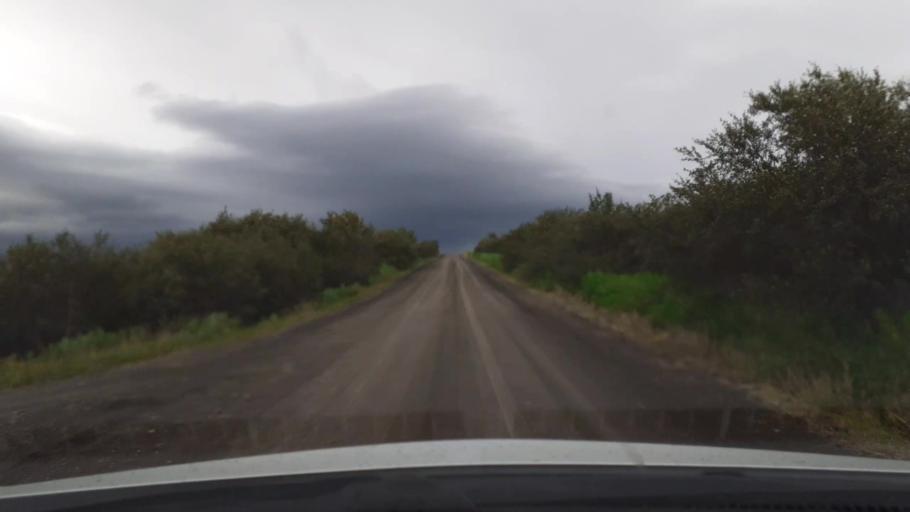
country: IS
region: Capital Region
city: Mosfellsbaer
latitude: 64.5238
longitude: -21.4734
